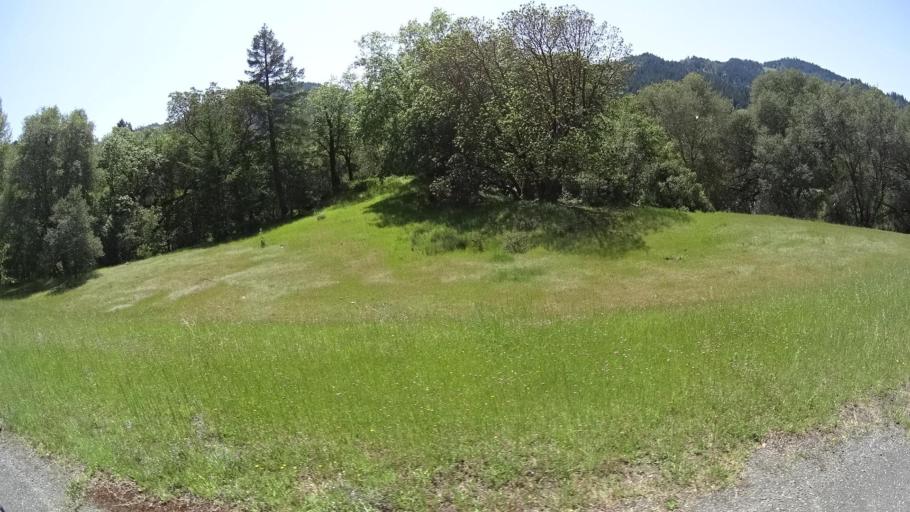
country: US
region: California
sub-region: Humboldt County
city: Redway
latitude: 40.2202
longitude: -123.6328
